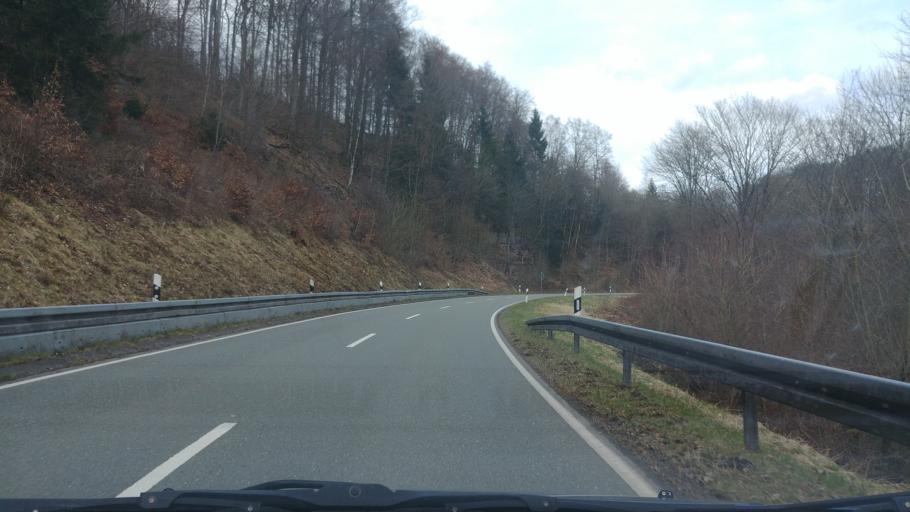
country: DE
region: Lower Saxony
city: Furstenberg
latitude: 51.7447
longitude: 9.4289
